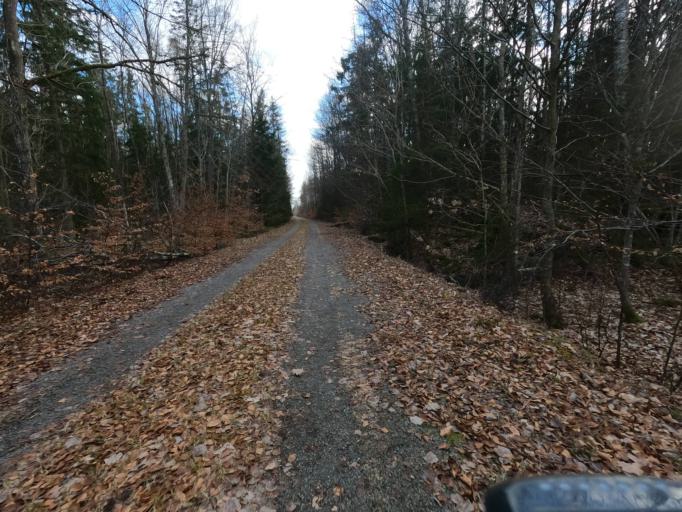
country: SE
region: Kronoberg
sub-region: Vaxjo Kommun
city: Gemla
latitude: 56.6597
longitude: 14.6192
